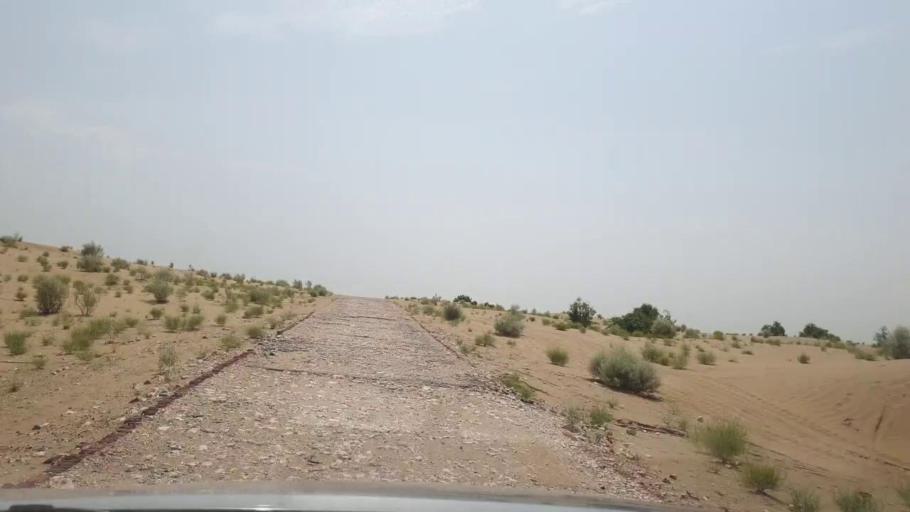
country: PK
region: Sindh
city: Pano Aqil
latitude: 27.5821
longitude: 69.1670
